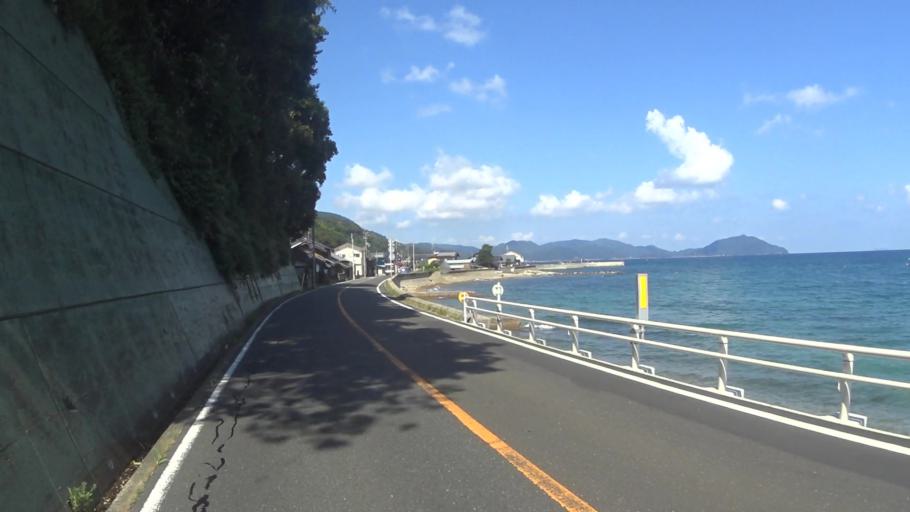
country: JP
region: Kyoto
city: Miyazu
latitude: 35.6229
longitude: 135.2450
